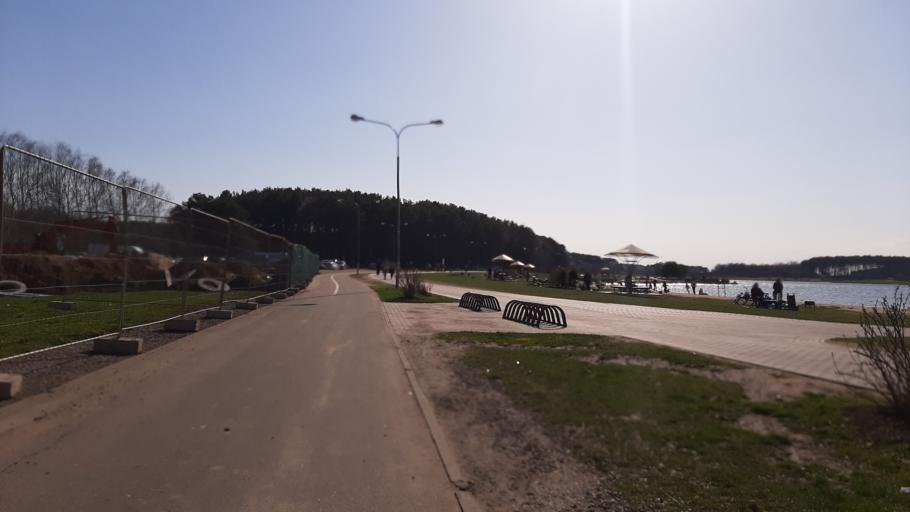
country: BY
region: Minsk
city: Bal'shavik
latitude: 53.9540
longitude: 27.5841
